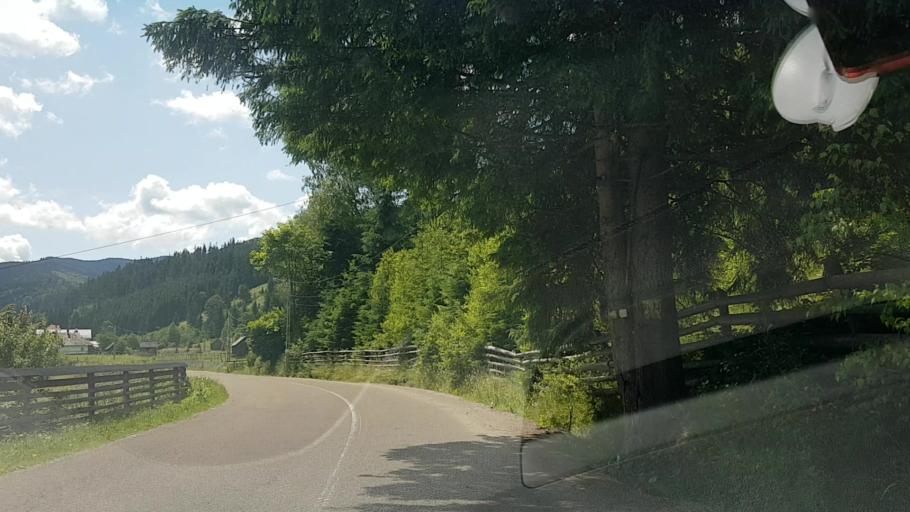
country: RO
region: Suceava
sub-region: Comuna Pojorata
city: Pojorata
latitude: 47.4963
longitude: 25.4821
